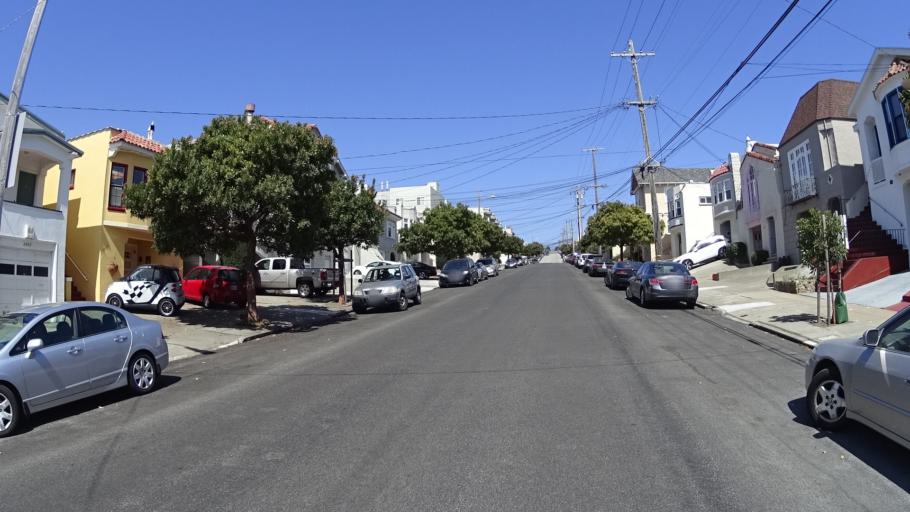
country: US
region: California
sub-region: San Mateo County
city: Daly City
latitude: 37.7416
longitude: -122.4820
